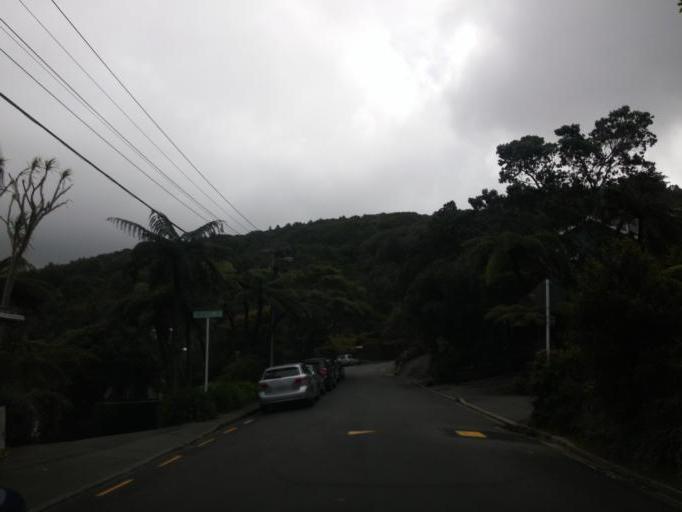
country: NZ
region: Wellington
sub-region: Wellington City
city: Wellington
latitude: -41.2435
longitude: 174.7876
